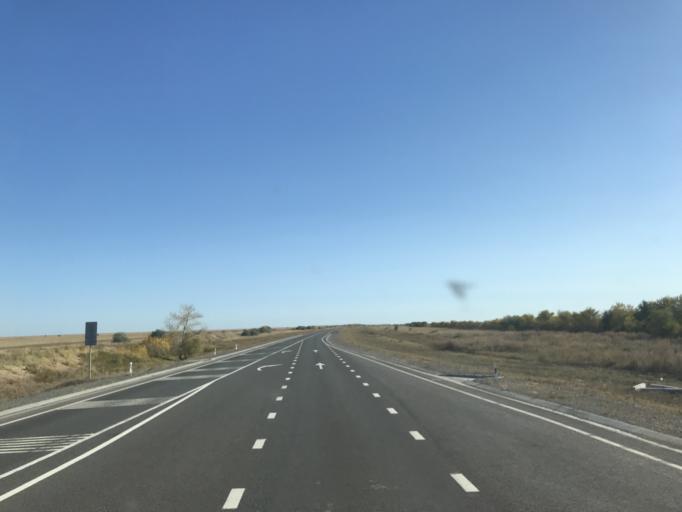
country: KZ
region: Pavlodar
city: Aksu
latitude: 52.0147
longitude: 77.2381
